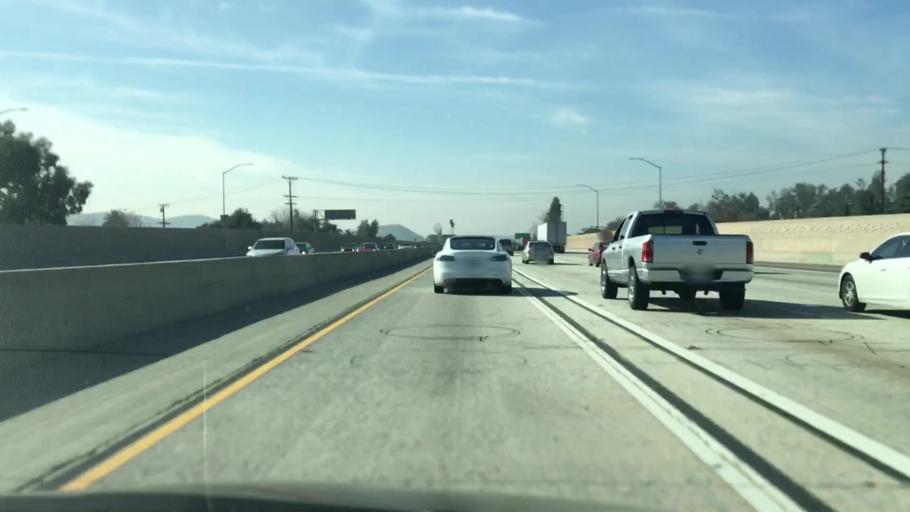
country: US
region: California
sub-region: Los Angeles County
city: Pomona
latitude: 34.0733
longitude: -117.7539
